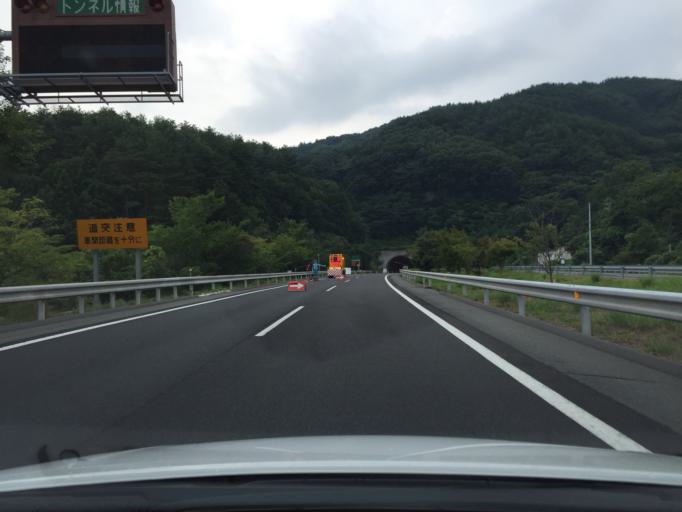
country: JP
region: Fukushima
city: Iwaki
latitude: 37.1296
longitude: 140.7540
